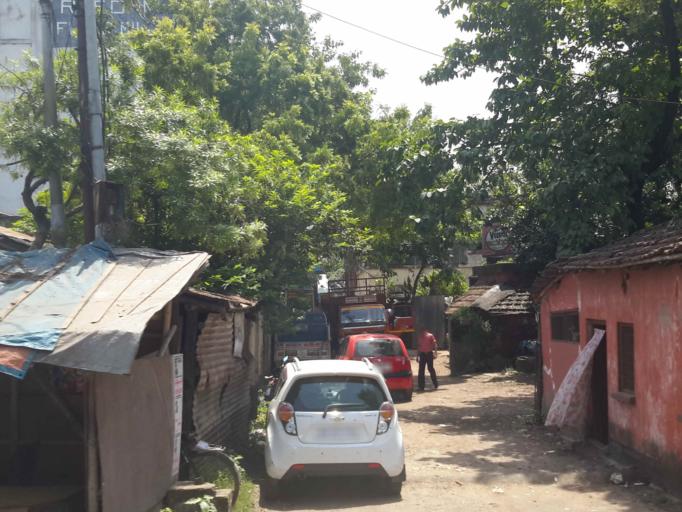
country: IN
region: West Bengal
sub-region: Haora
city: Haora
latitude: 22.5707
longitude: 88.3322
